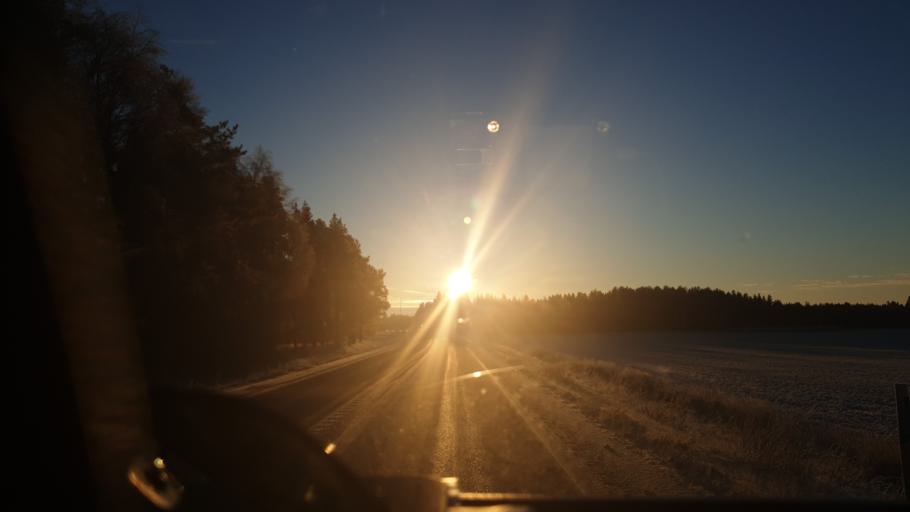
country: FI
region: Northern Ostrobothnia
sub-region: Ylivieska
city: Kalajoki
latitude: 64.2965
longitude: 23.9394
